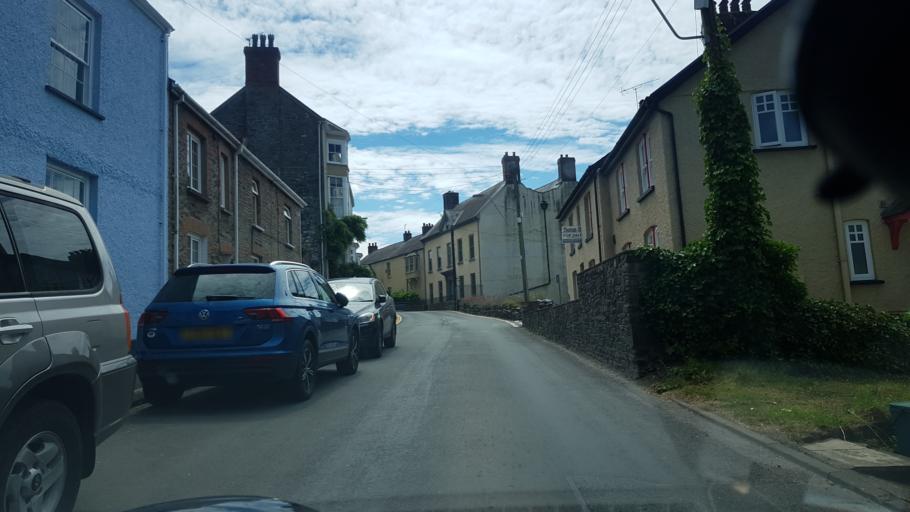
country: GB
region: Wales
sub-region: Carmarthenshire
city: Saint Clears
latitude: 51.7732
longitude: -4.4631
